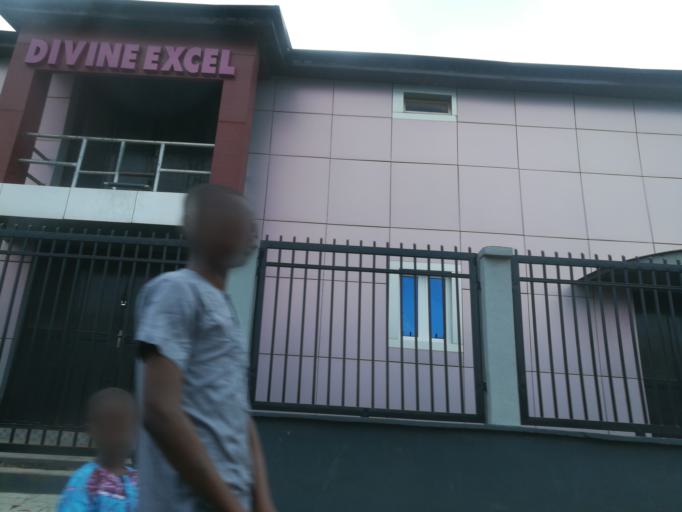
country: NG
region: Lagos
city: Agege
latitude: 6.6078
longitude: 3.3161
